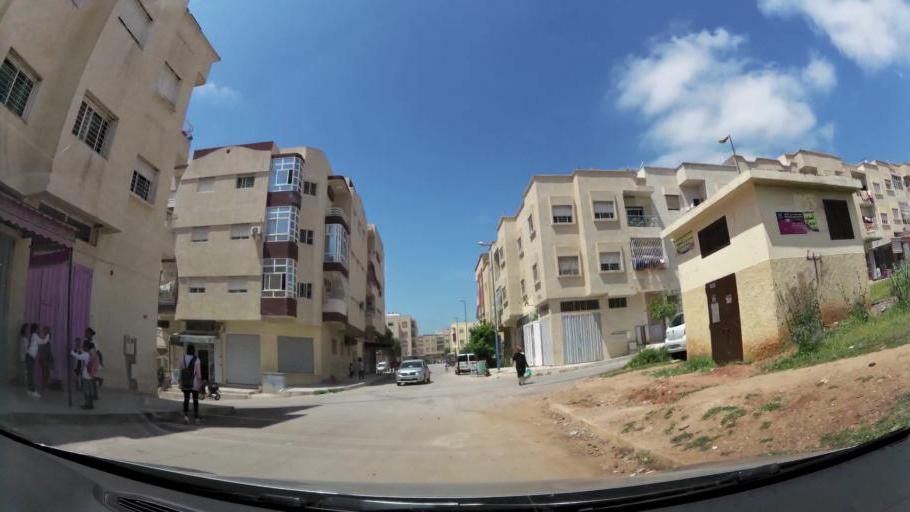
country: MA
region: Fes-Boulemane
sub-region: Fes
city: Fes
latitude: 34.0614
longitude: -5.0210
